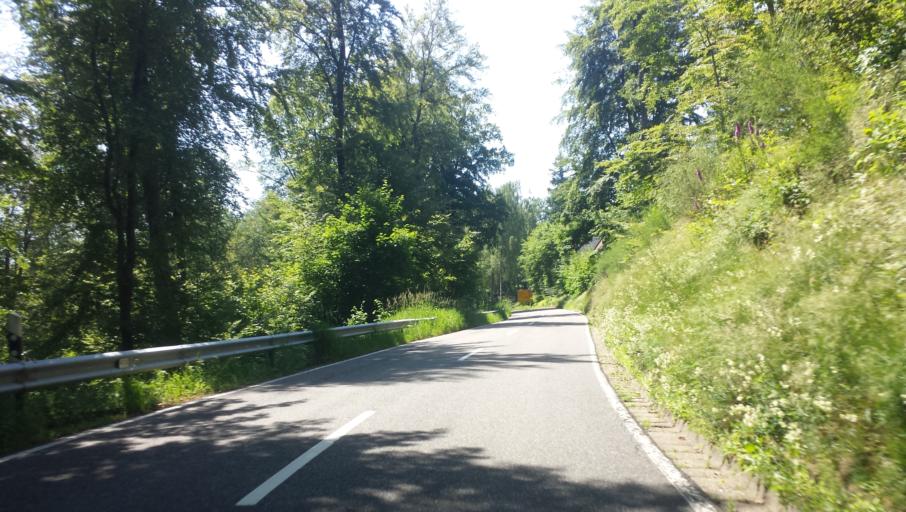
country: DE
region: Rheinland-Pfalz
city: Trippstadt
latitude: 49.3372
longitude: 7.8271
